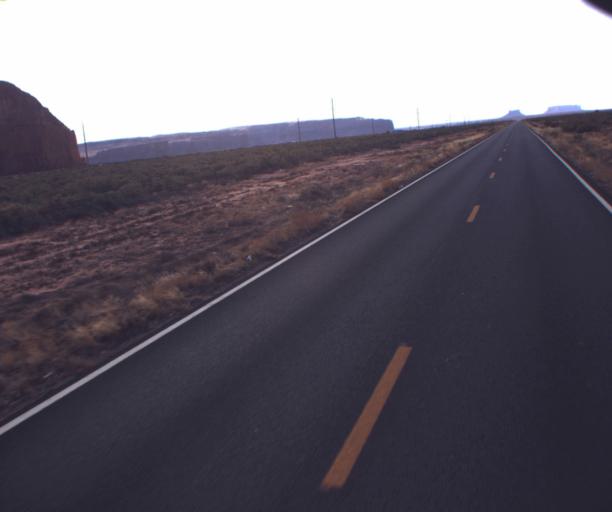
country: US
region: Arizona
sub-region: Apache County
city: Many Farms
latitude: 36.6674
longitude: -109.5981
